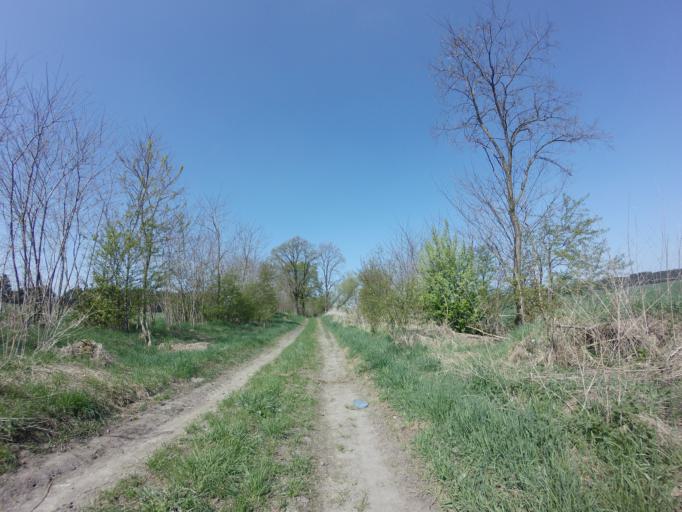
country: PL
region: West Pomeranian Voivodeship
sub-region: Powiat choszczenski
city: Choszczno
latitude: 53.2076
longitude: 15.3610
